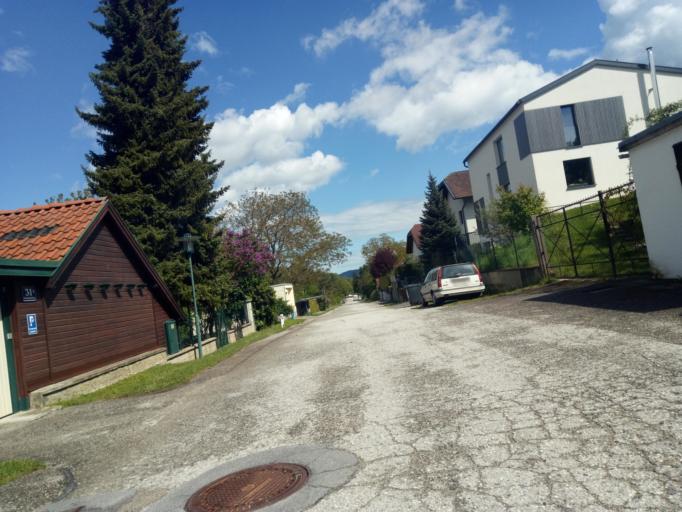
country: AT
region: Lower Austria
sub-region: Politischer Bezirk Modling
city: Breitenfurt bei Wien
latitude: 48.1396
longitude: 16.1397
